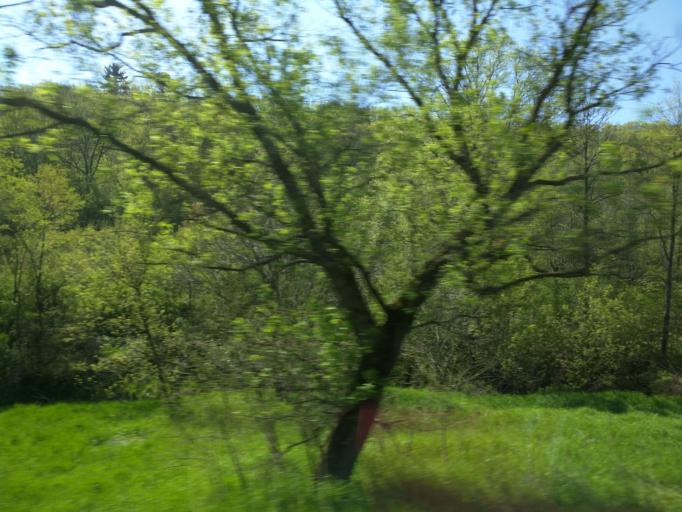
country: US
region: Wisconsin
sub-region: Monroe County
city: Cashton
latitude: 43.6413
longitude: -90.6492
